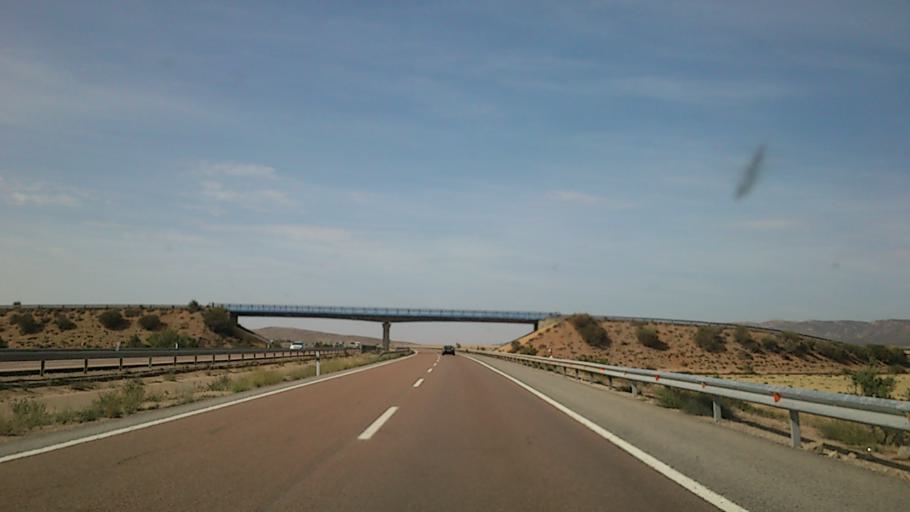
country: ES
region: Aragon
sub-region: Provincia de Teruel
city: Santa Eulalia
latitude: 40.6036
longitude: -1.2856
